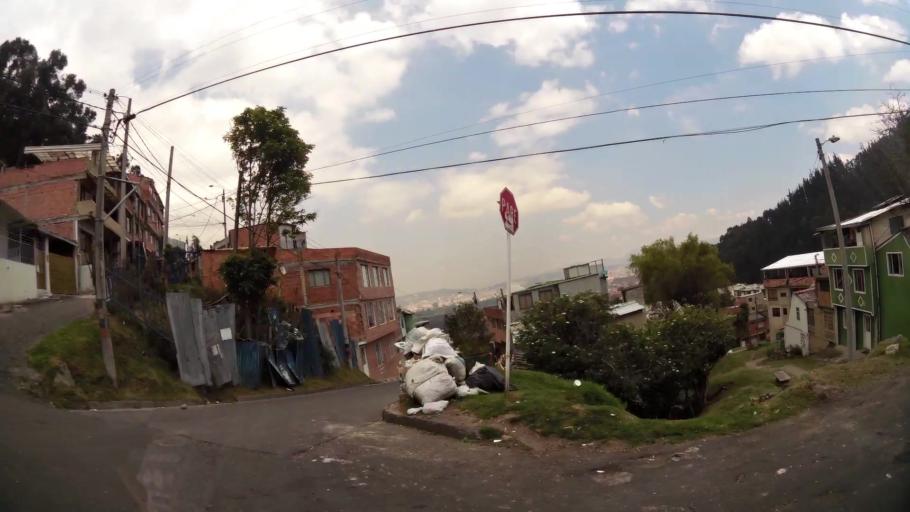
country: CO
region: Bogota D.C.
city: Barrio San Luis
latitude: 4.7035
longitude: -74.0237
